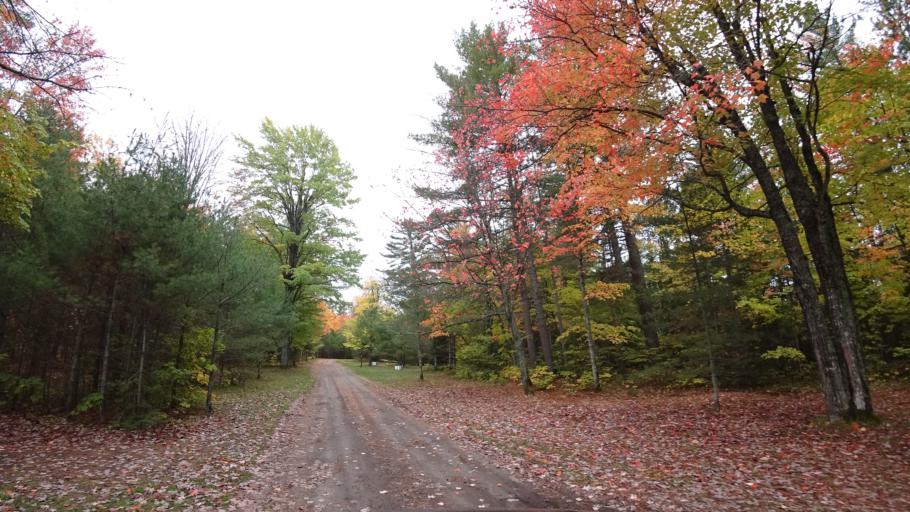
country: US
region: Michigan
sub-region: Marquette County
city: West Ishpeming
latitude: 46.5310
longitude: -88.0003
